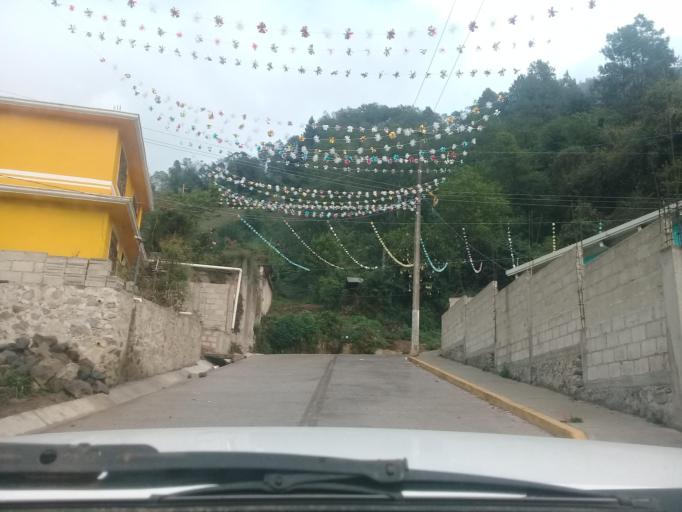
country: MX
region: Veracruz
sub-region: Mariano Escobedo
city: San Isidro el Berro
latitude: 18.9561
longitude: -97.1966
